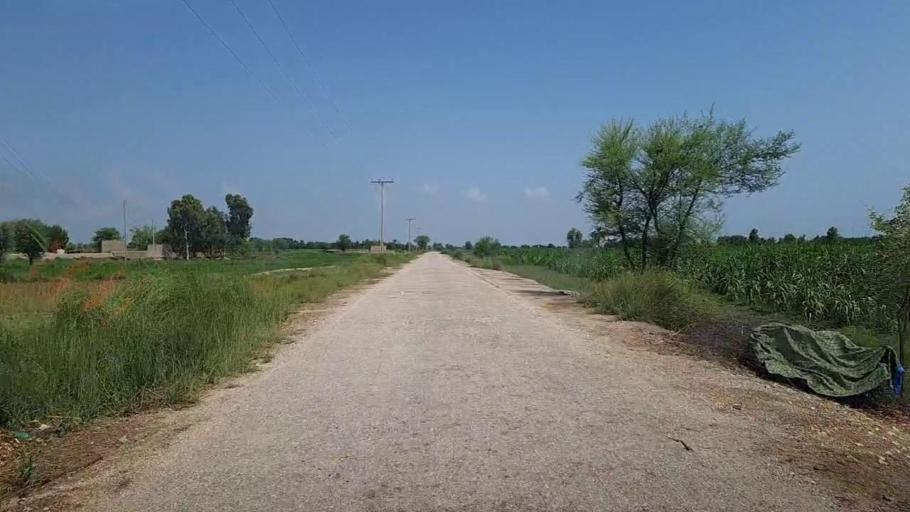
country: PK
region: Sindh
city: Bhiria
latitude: 26.8830
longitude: 68.2382
